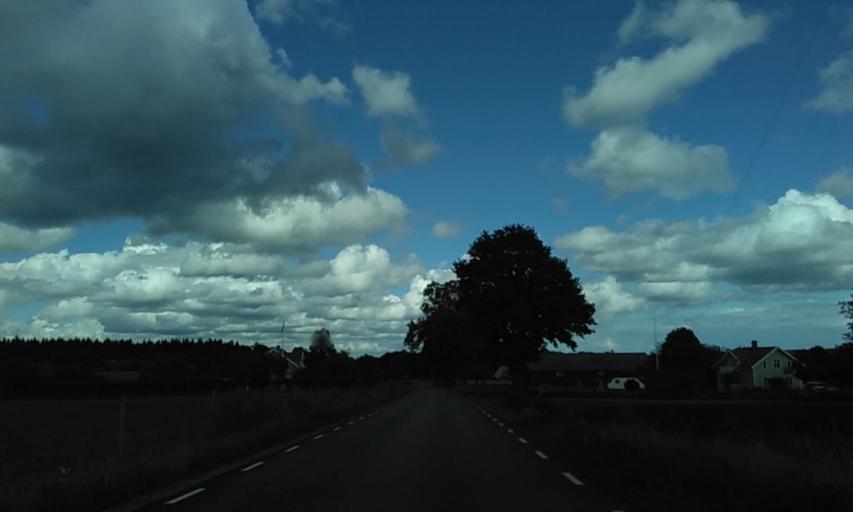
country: SE
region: Vaestra Goetaland
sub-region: Vargarda Kommun
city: Vargarda
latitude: 57.9828
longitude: 12.9181
